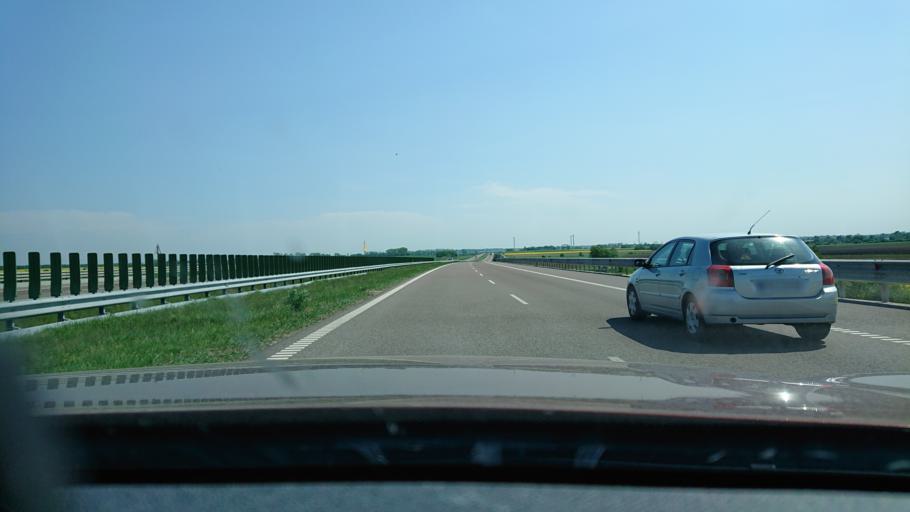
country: PL
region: Subcarpathian Voivodeship
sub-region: Powiat przemyski
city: Stubno
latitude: 49.9409
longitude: 22.9541
